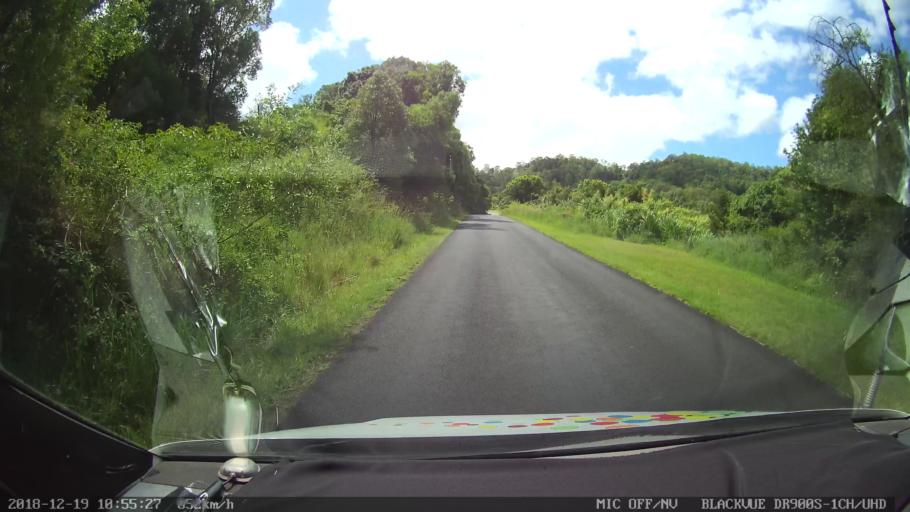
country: AU
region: New South Wales
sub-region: Lismore Municipality
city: Nimbin
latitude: -28.5946
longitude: 153.2545
